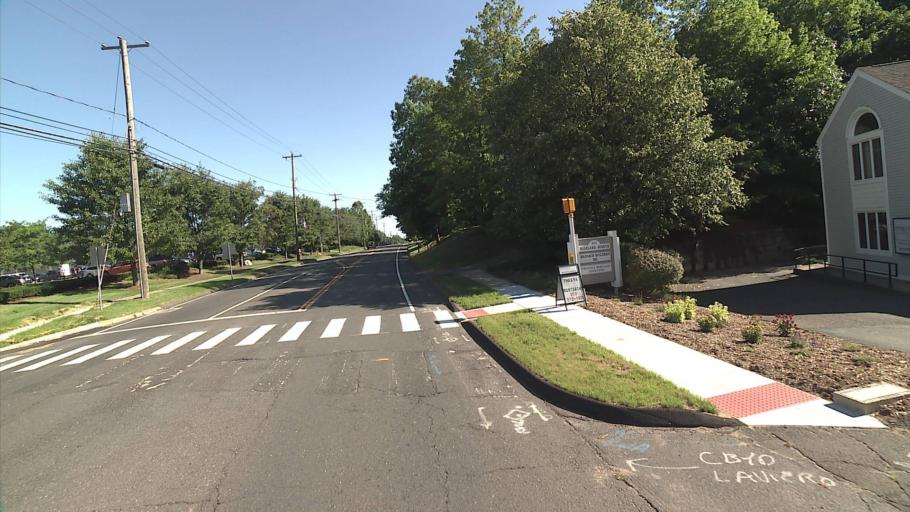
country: US
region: Connecticut
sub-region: New Haven County
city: Cheshire Village
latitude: 41.5048
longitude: -72.9005
